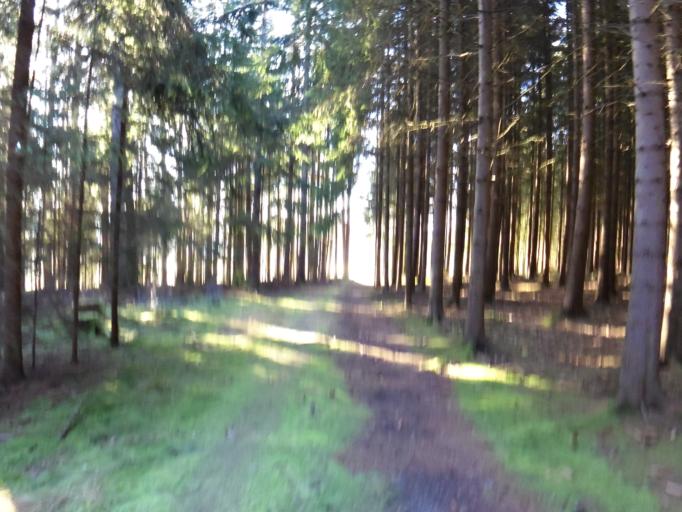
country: DE
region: Bavaria
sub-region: Upper Franconia
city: Wunsiedel
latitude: 50.0652
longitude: 12.0374
